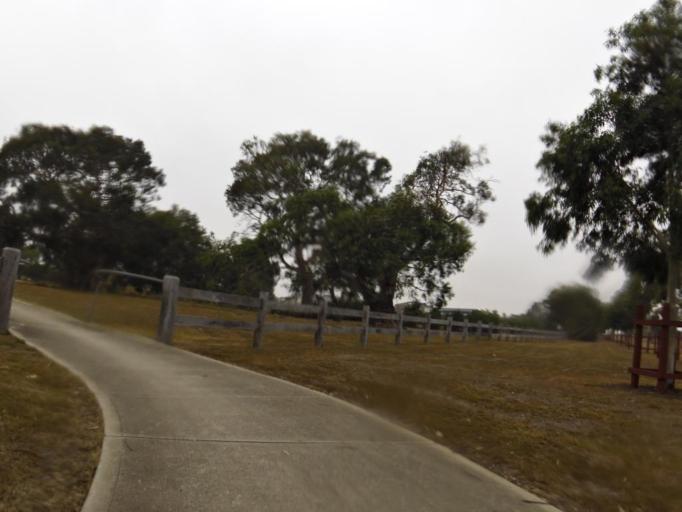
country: AU
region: Victoria
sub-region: Melton
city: Kurunjang
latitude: -37.6791
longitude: 144.5990
